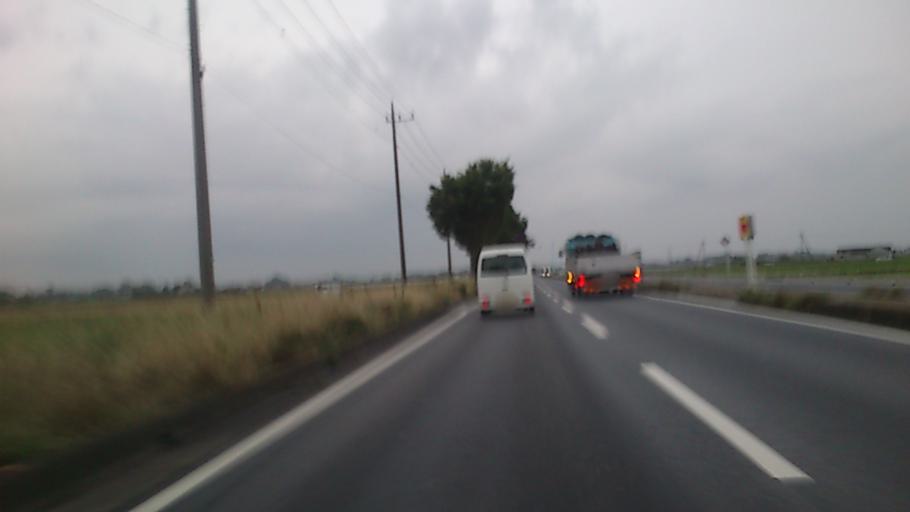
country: JP
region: Saitama
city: Hanyu
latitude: 36.1539
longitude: 139.5044
